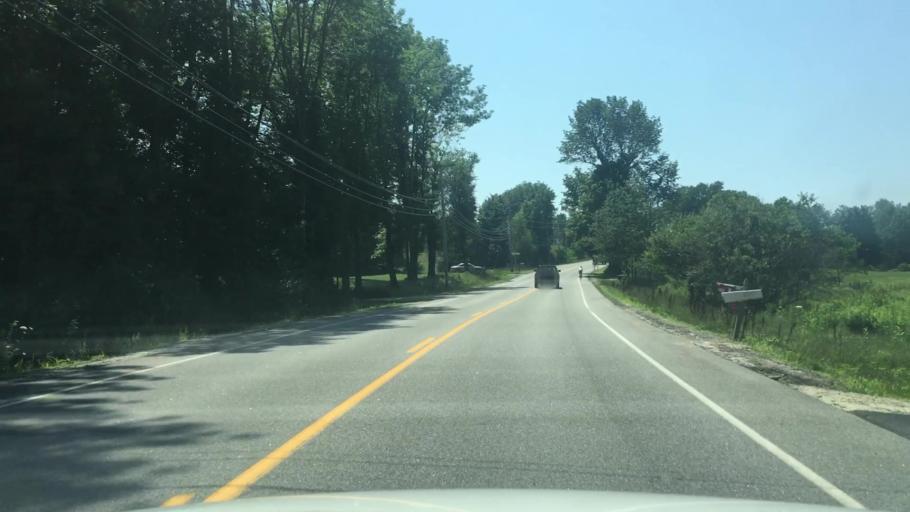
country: US
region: Maine
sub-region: Cumberland County
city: Cumberland Center
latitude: 43.8153
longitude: -70.2894
